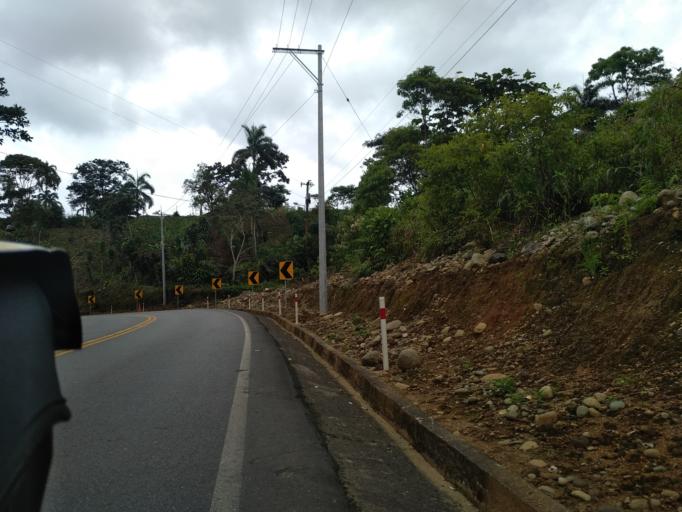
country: EC
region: Pastaza
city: Puyo
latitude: -1.3044
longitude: -77.8828
